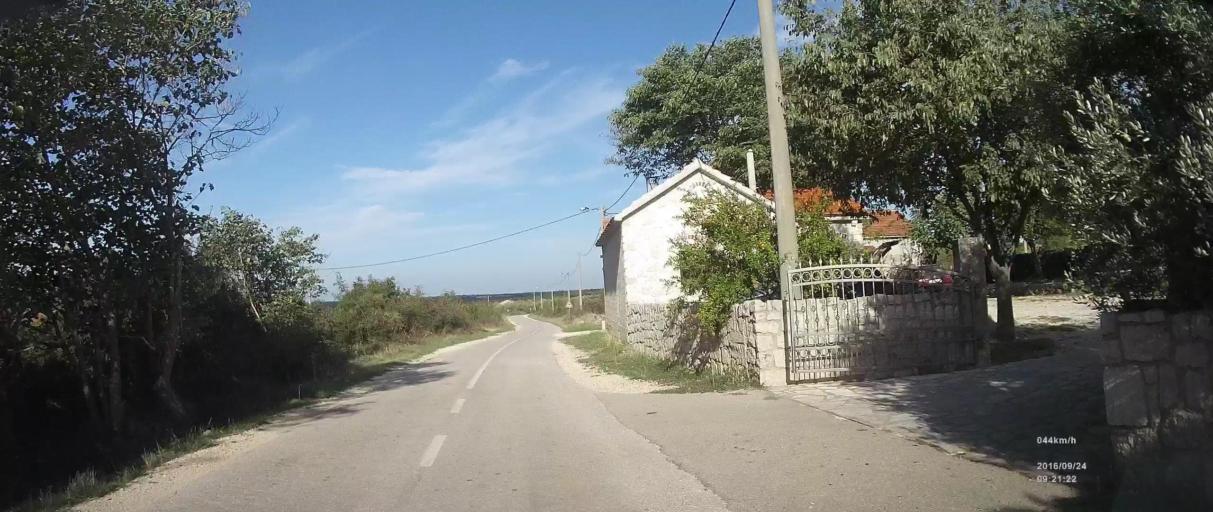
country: HR
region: Zadarska
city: Polaca
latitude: 44.0689
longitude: 15.4891
